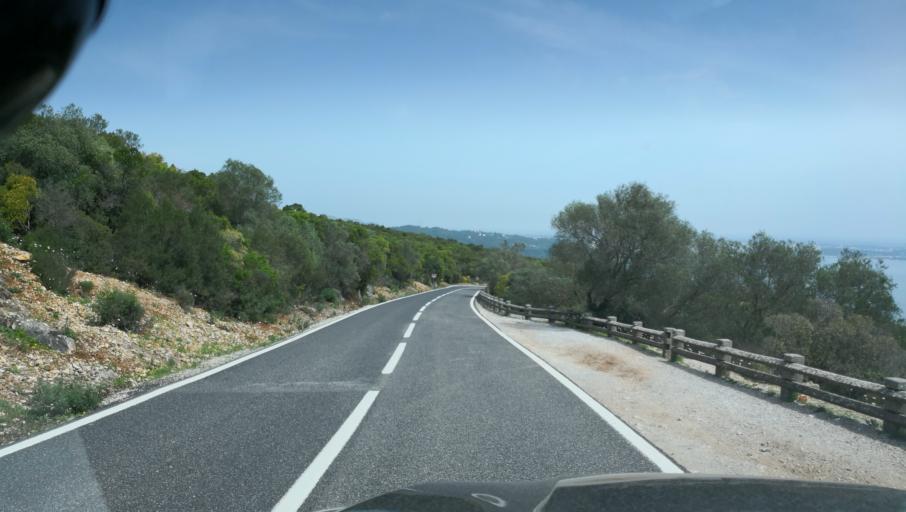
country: PT
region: Setubal
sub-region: Setubal
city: Setubal
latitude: 38.4894
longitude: -8.9406
